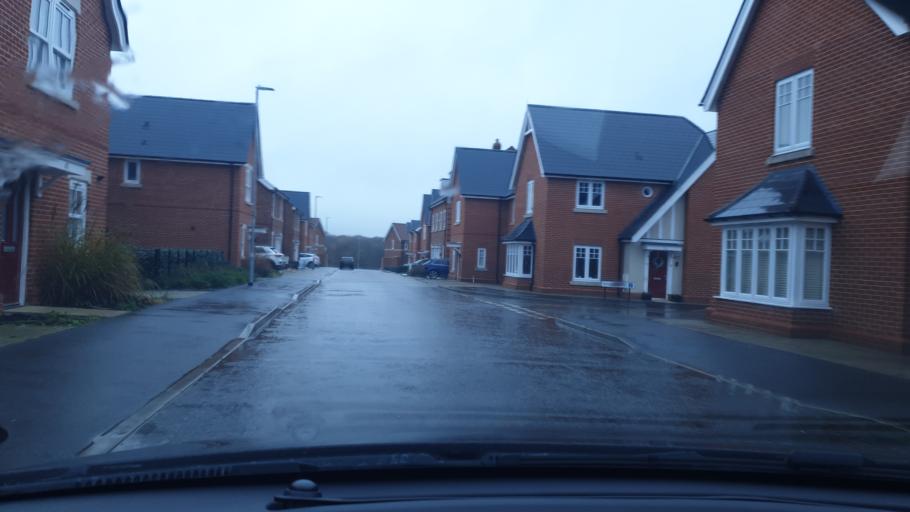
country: GB
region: England
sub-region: Essex
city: Great Horkesley
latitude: 51.9178
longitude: 0.8813
